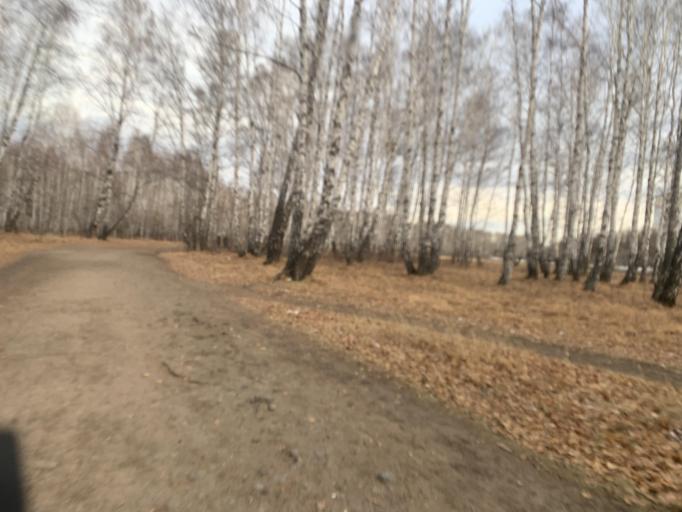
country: RU
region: Chelyabinsk
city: Roshchino
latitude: 55.2004
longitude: 61.3038
